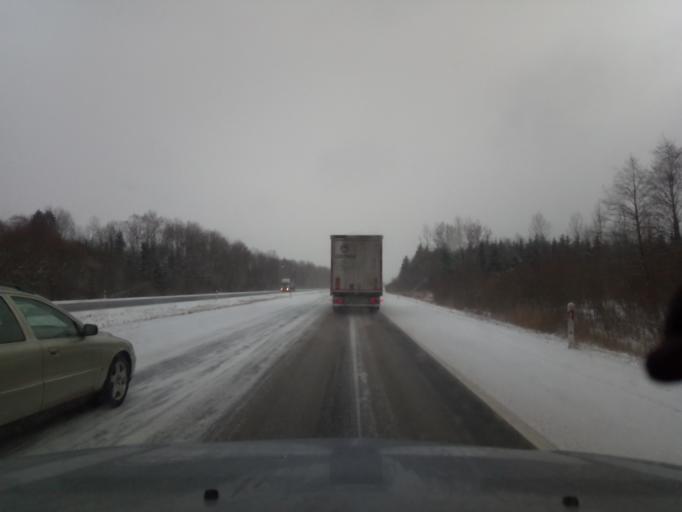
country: LT
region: Vilnius County
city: Ukmerge
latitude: 55.4652
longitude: 24.6599
